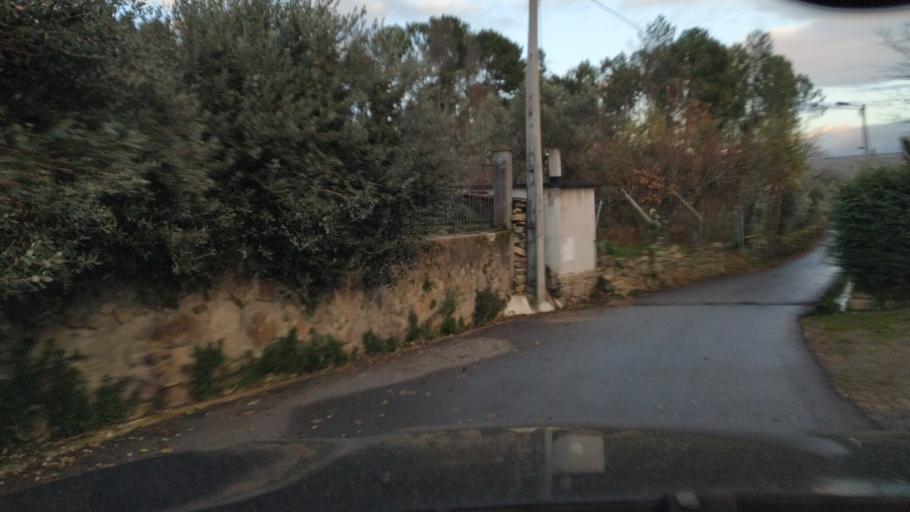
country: PT
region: Vila Real
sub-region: Vila Real
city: Vila Real
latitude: 41.3468
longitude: -7.7216
